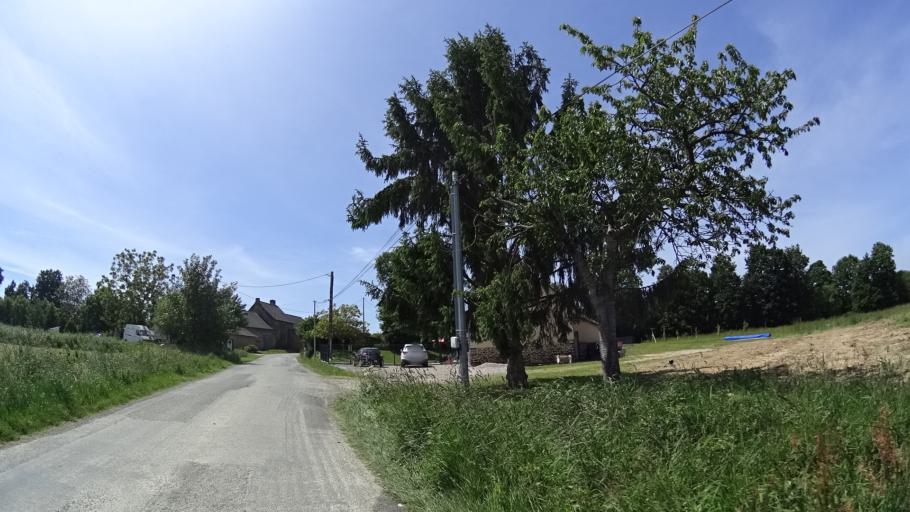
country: FR
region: Brittany
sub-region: Departement d'Ille-et-Vilaine
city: Montfort-sur-Meu
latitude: 48.1564
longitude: -1.9824
